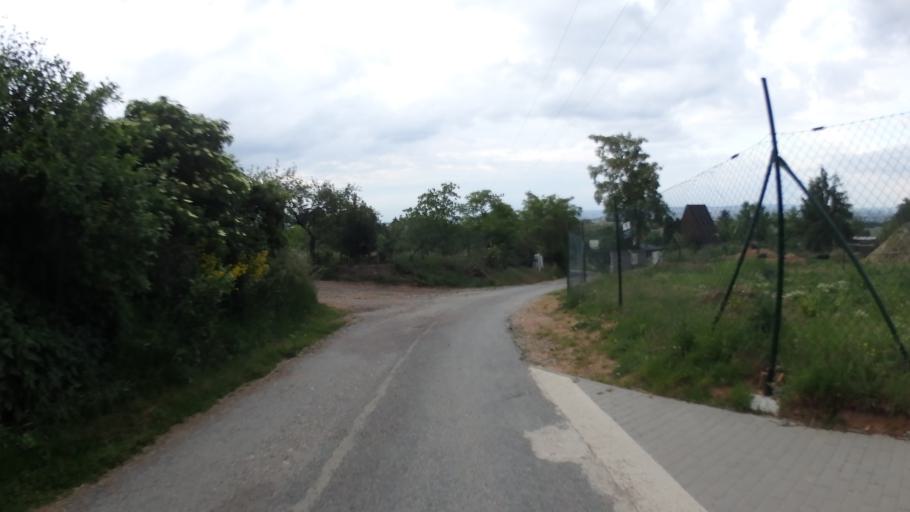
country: CZ
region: South Moravian
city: Ostopovice
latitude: 49.1355
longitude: 16.5457
